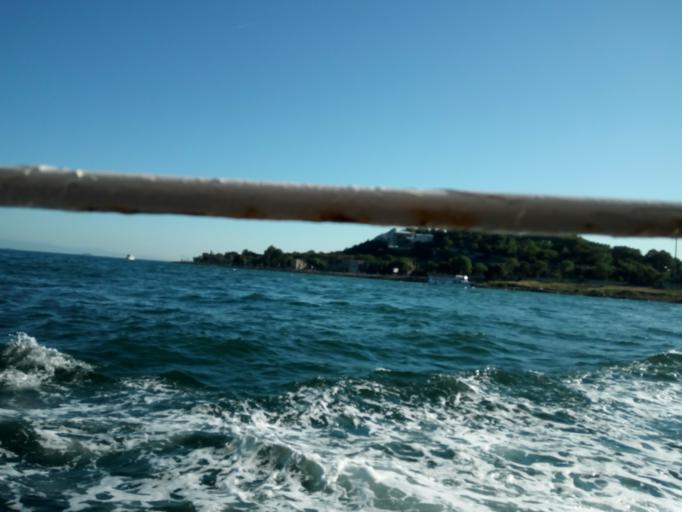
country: TR
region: Istanbul
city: Eminoenue
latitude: 41.0179
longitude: 28.9902
